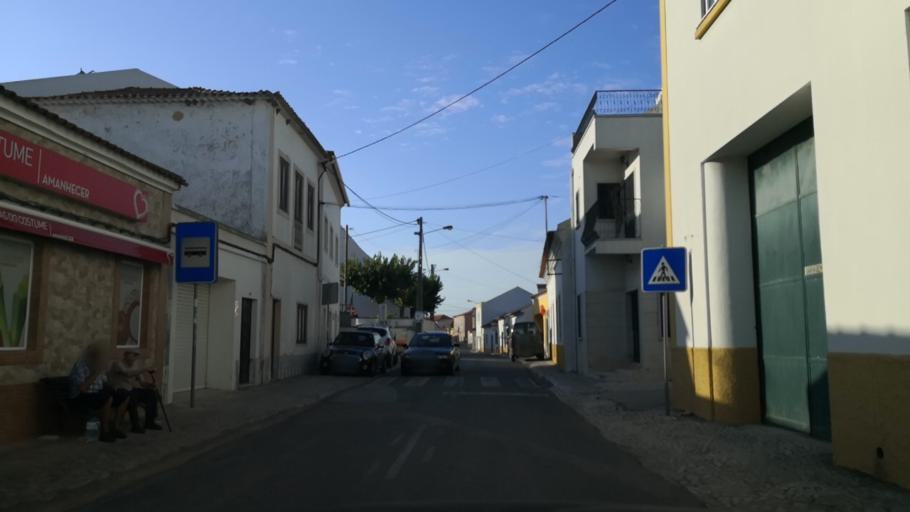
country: PT
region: Santarem
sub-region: Santarem
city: Santarem
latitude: 39.2954
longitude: -8.6580
